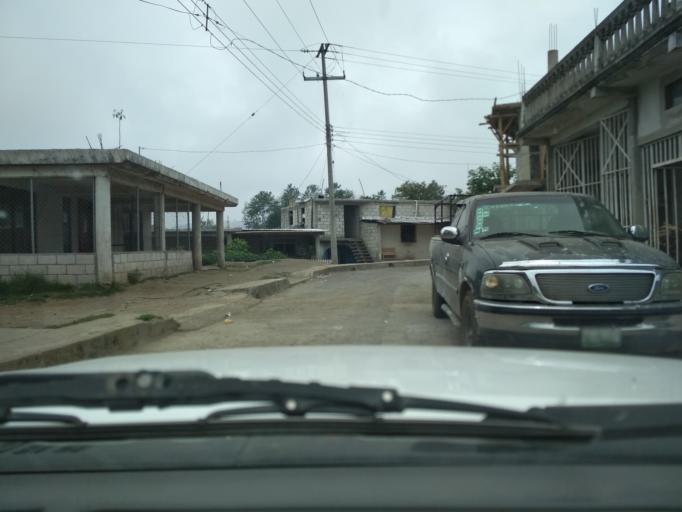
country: MX
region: Veracruz
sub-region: La Perla
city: Chilapa
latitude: 18.9882
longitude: -97.1504
